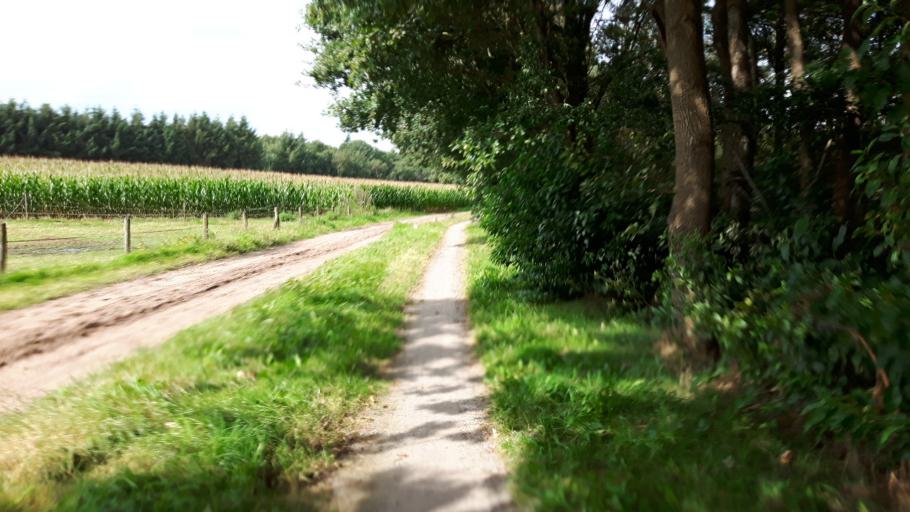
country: NL
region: Groningen
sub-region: Gemeente Leek
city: Leek
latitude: 53.1066
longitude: 6.4014
